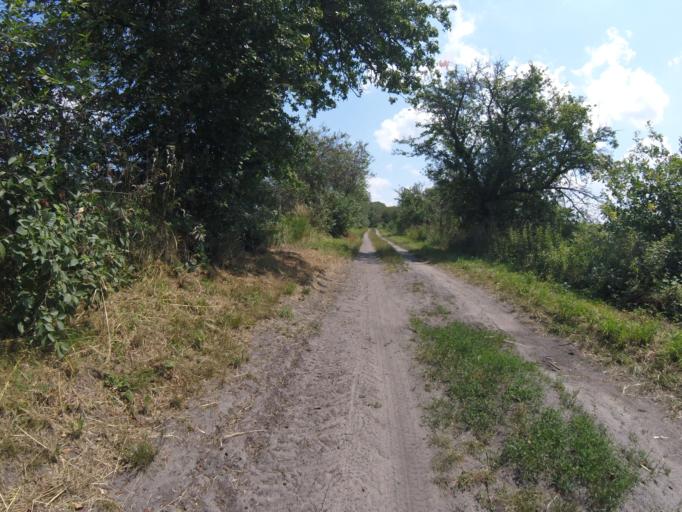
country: DE
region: Brandenburg
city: Bestensee
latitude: 52.2664
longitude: 13.7042
